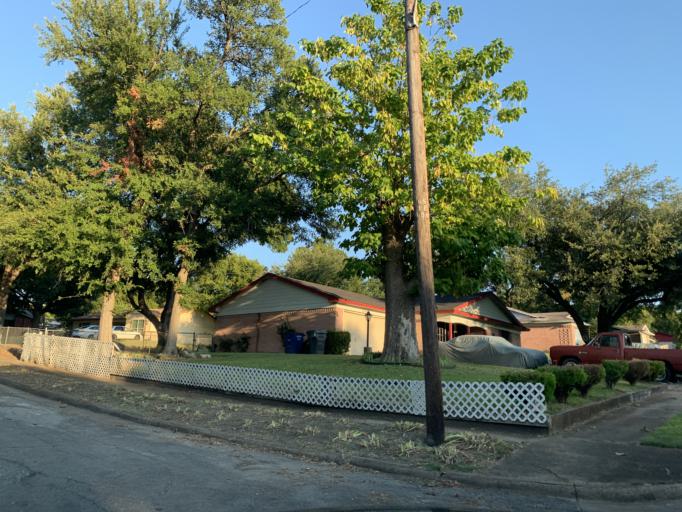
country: US
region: Texas
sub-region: Dallas County
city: Lancaster
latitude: 32.6647
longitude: -96.8041
